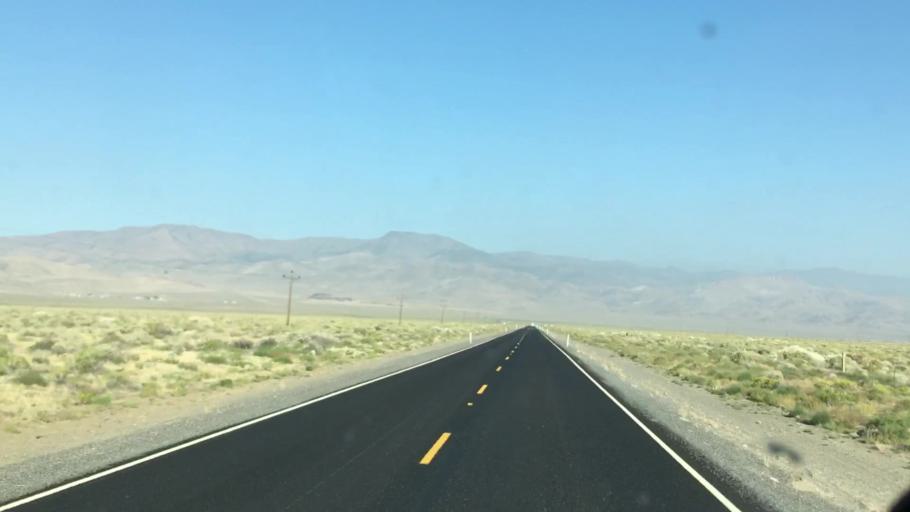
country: US
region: Nevada
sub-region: Lyon County
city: Fernley
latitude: 39.6451
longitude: -119.3098
